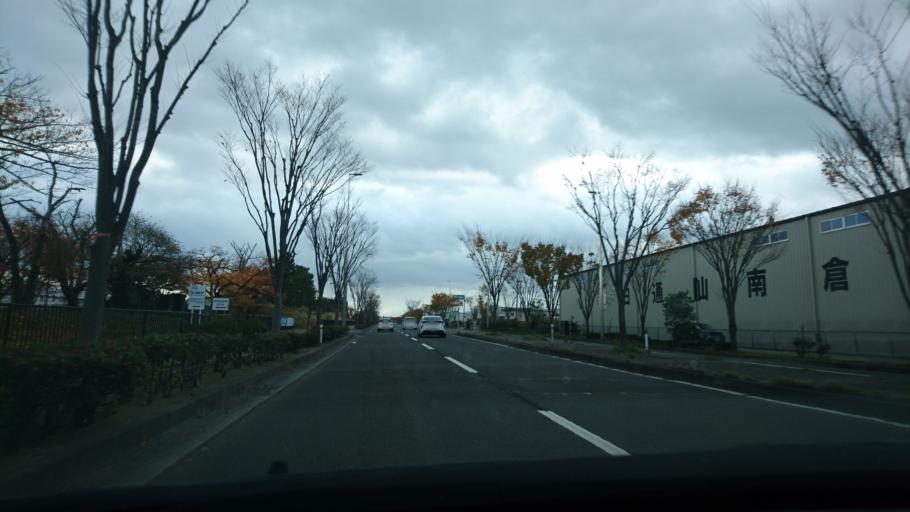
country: JP
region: Miyagi
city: Iwanuma
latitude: 38.1333
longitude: 140.9135
